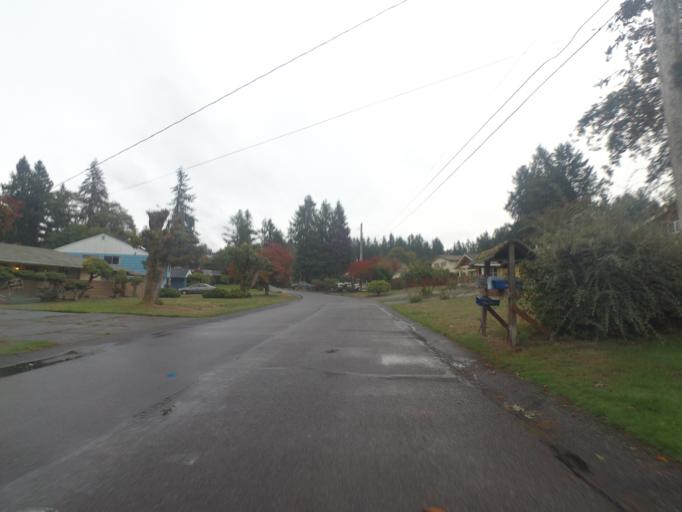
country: US
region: Washington
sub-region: Pierce County
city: University Place
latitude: 47.2189
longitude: -122.5585
